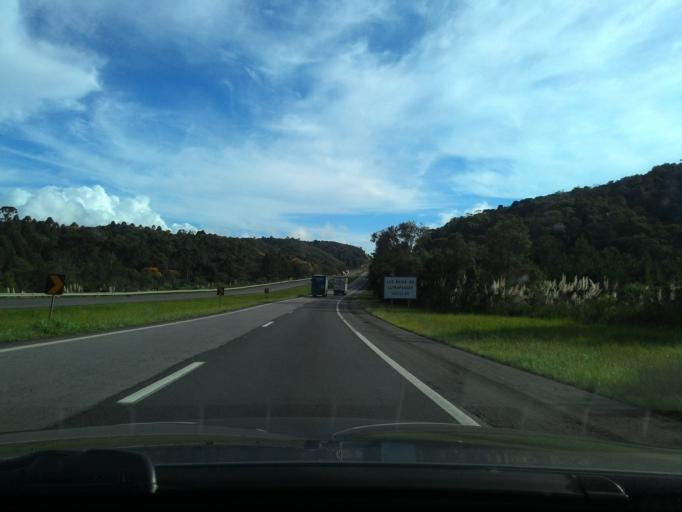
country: BR
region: Parana
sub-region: Campina Grande Do Sul
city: Campina Grande do Sul
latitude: -25.2630
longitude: -48.9149
